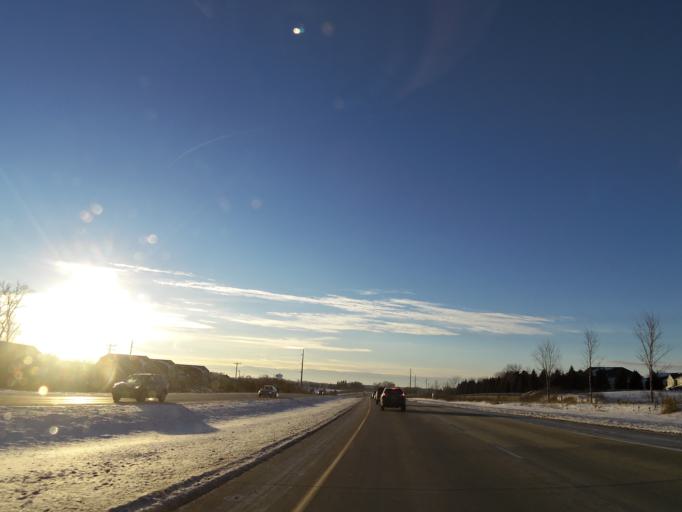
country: US
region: Minnesota
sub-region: Carver County
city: Chanhassen
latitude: 44.8633
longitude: -93.5698
